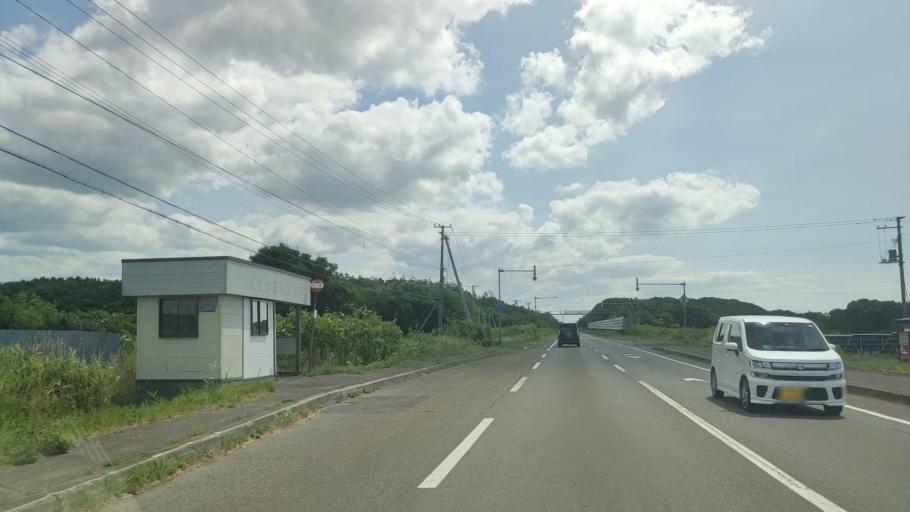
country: JP
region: Hokkaido
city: Makubetsu
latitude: 44.7700
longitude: 141.7926
